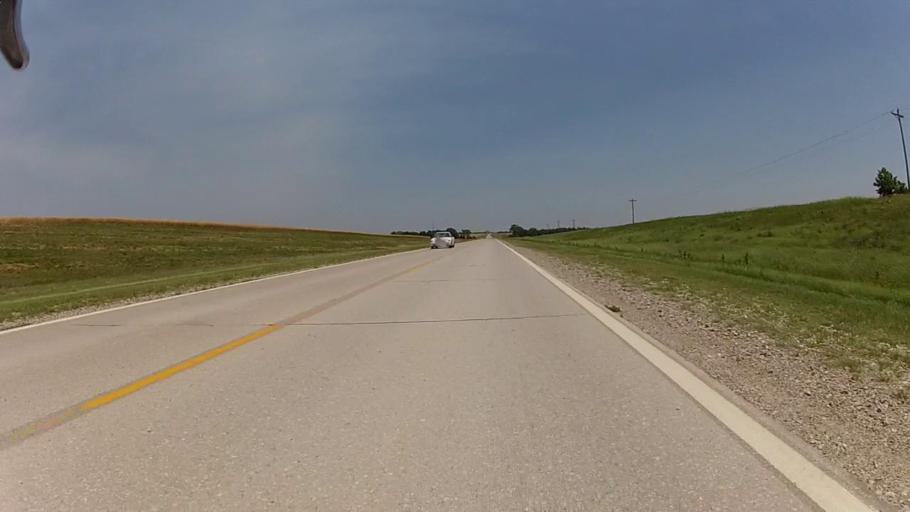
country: US
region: Kansas
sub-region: Sumner County
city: Wellington
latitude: 37.0572
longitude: -97.2954
